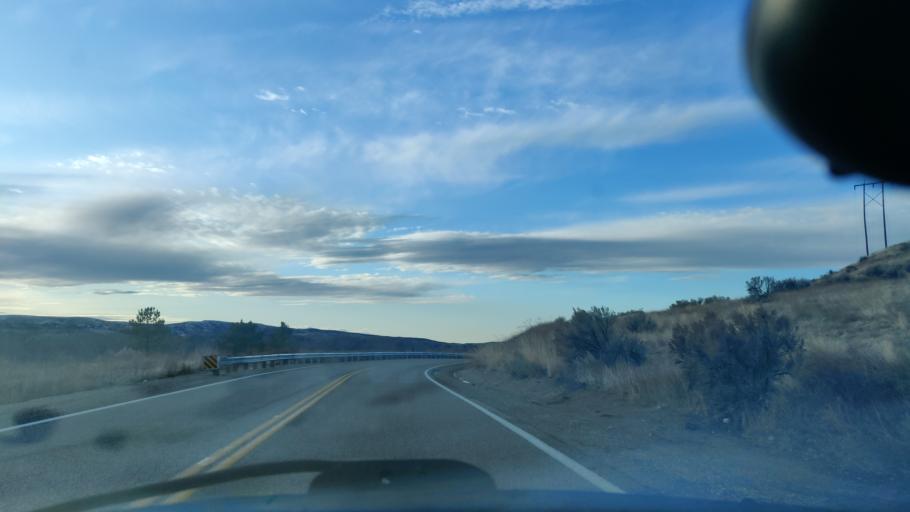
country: US
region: Idaho
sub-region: Ada County
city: Garden City
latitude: 43.7213
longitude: -116.2403
